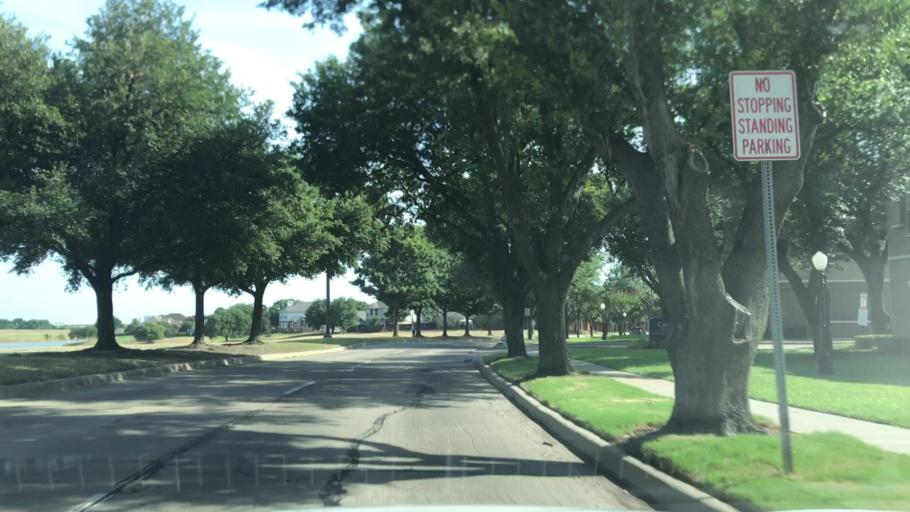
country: US
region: Texas
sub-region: Dallas County
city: Farmers Branch
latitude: 32.9336
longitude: -96.9436
